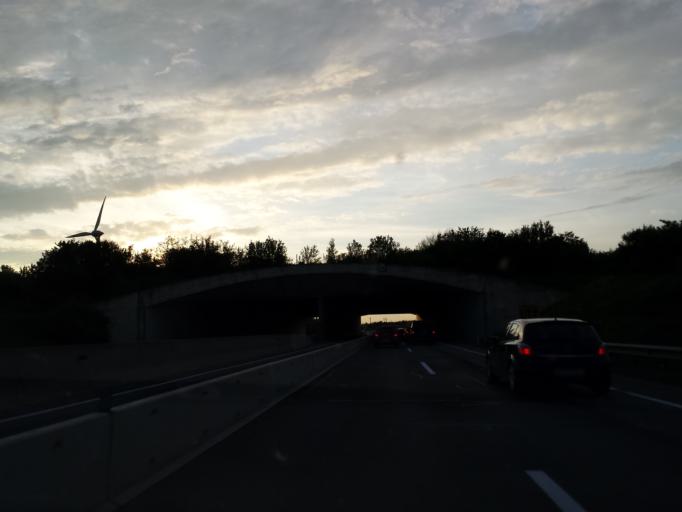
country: AT
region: Burgenland
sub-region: Politischer Bezirk Neusiedl am See
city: Gols
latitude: 47.9515
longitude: 16.9261
